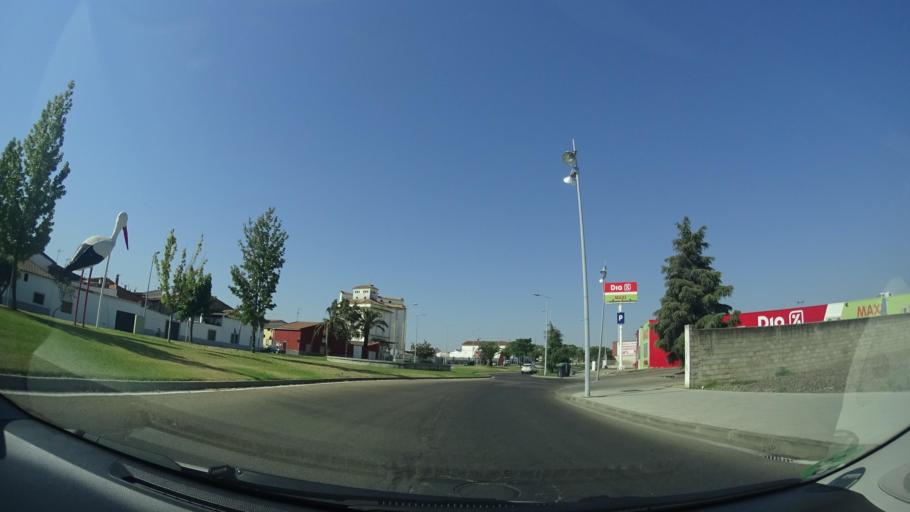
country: ES
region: Extremadura
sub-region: Provincia de Caceres
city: Miajadas
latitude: 39.1464
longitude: -5.9186
